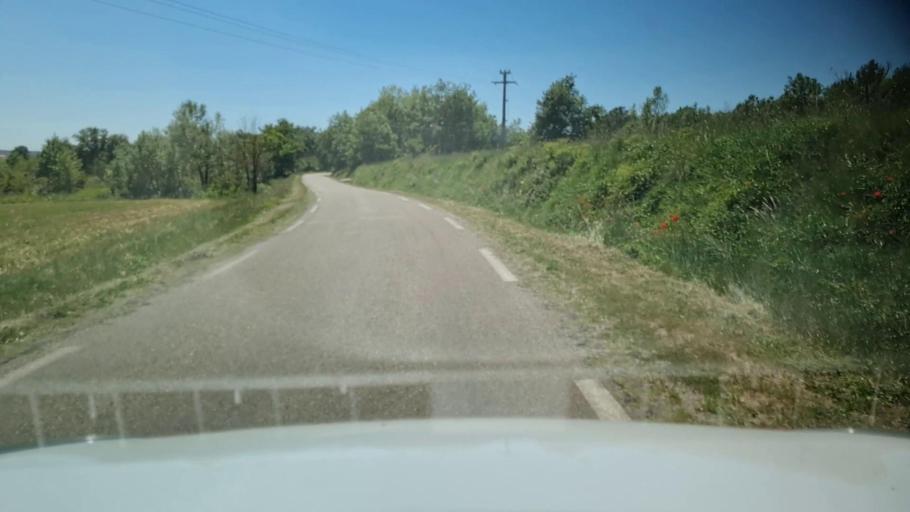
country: FR
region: Languedoc-Roussillon
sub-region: Departement du Gard
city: Saint-Mamert-du-Gard
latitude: 43.8965
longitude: 4.1893
